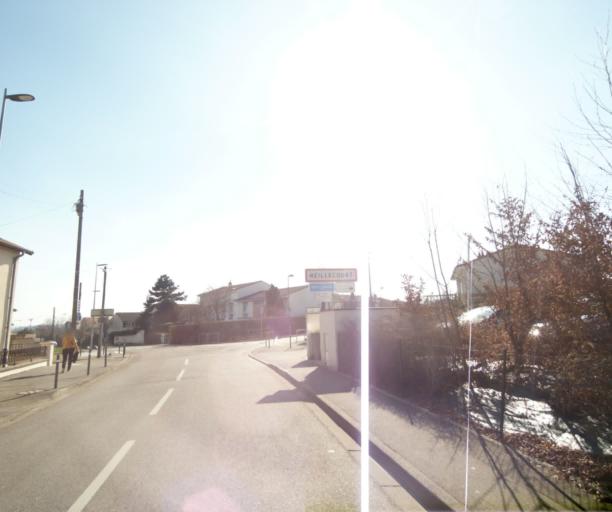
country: FR
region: Lorraine
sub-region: Departement de Meurthe-et-Moselle
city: Heillecourt
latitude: 48.6602
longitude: 6.1973
